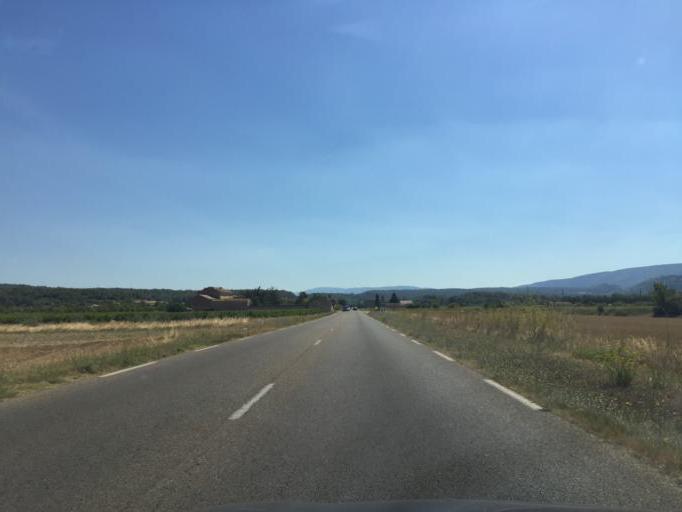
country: FR
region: Provence-Alpes-Cote d'Azur
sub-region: Departement du Vaucluse
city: Menerbes
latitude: 43.8615
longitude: 5.1814
